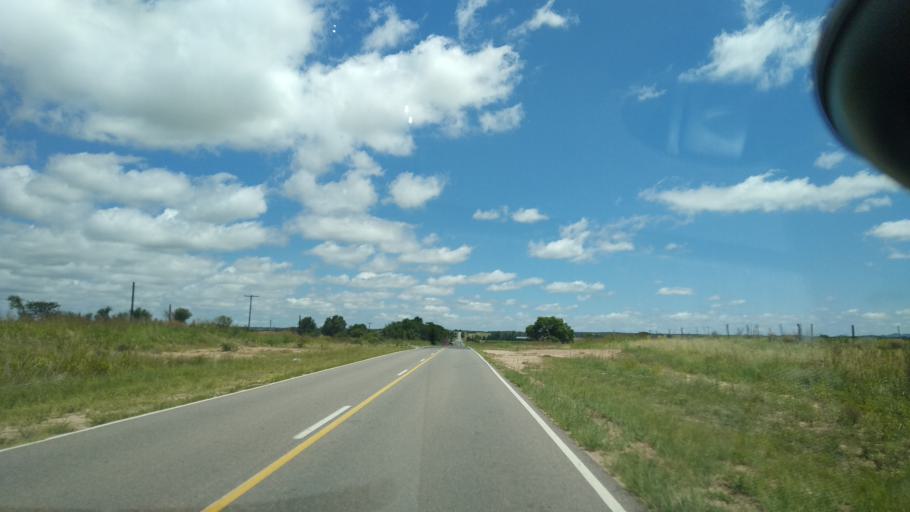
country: AR
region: Cordoba
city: Villa Cura Brochero
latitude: -31.6479
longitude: -65.1005
